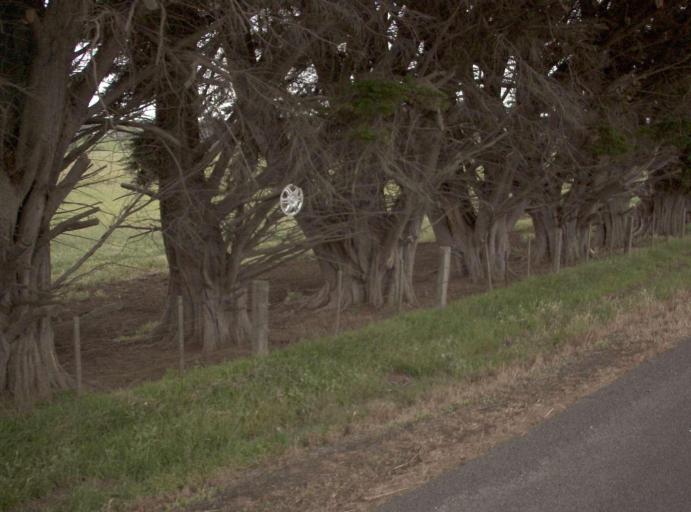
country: AU
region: Victoria
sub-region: Baw Baw
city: Warragul
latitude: -38.5099
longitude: 145.9519
